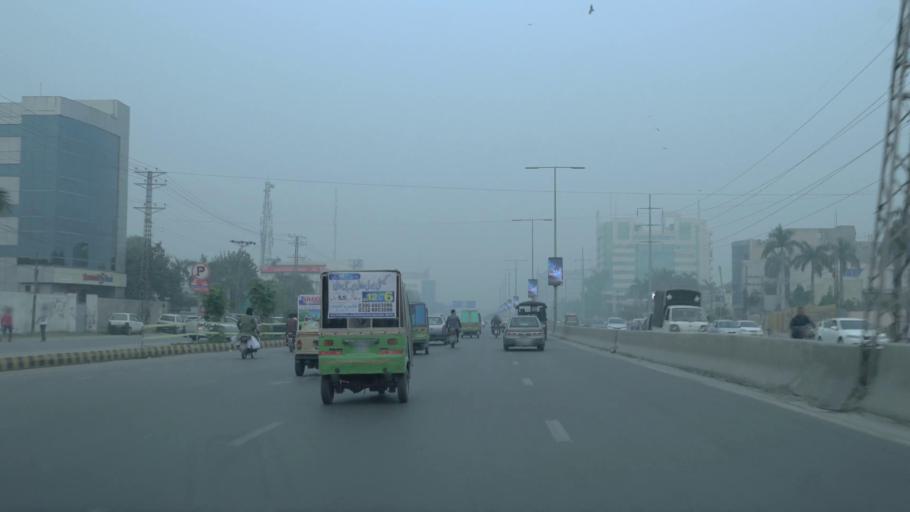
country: PK
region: Punjab
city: Lahore
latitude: 31.5018
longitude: 74.3225
